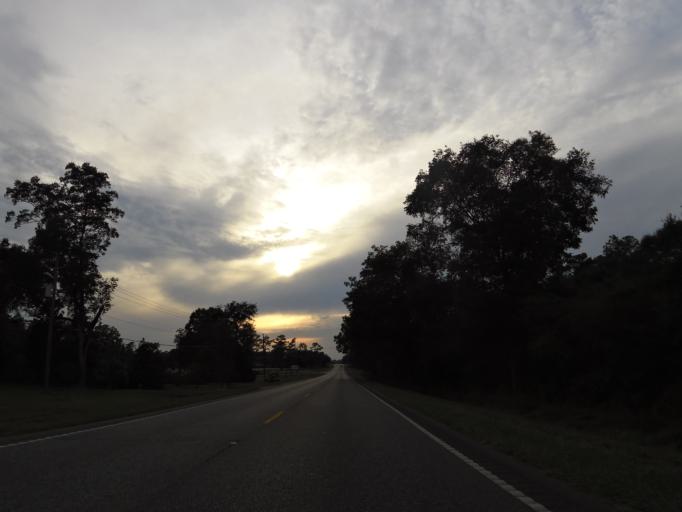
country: US
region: Alabama
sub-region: Escambia County
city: Atmore
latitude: 31.0234
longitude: -87.5111
